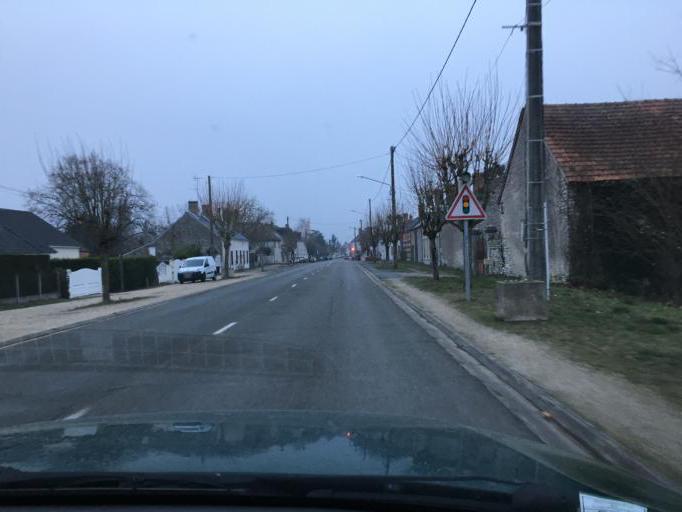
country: FR
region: Centre
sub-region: Departement du Loiret
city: Lailly-en-Val
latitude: 47.7700
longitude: 1.6920
